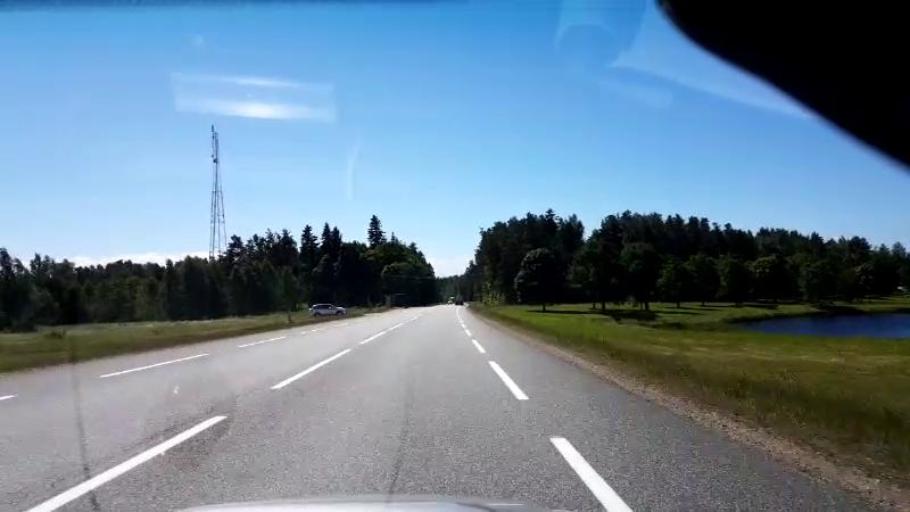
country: LV
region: Saulkrastu
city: Saulkrasti
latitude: 57.4036
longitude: 24.4302
